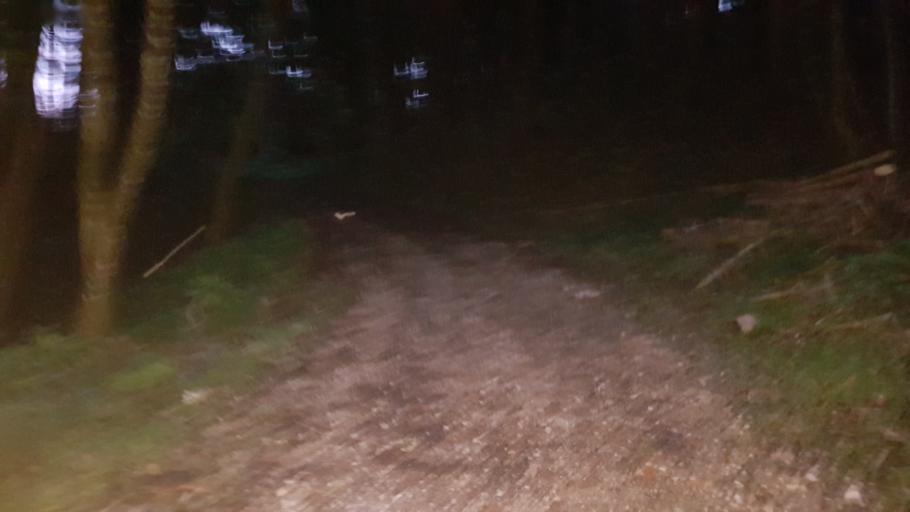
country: DE
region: Bavaria
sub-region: Upper Bavaria
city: Marktschellenberg
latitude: 47.7094
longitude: 13.0506
